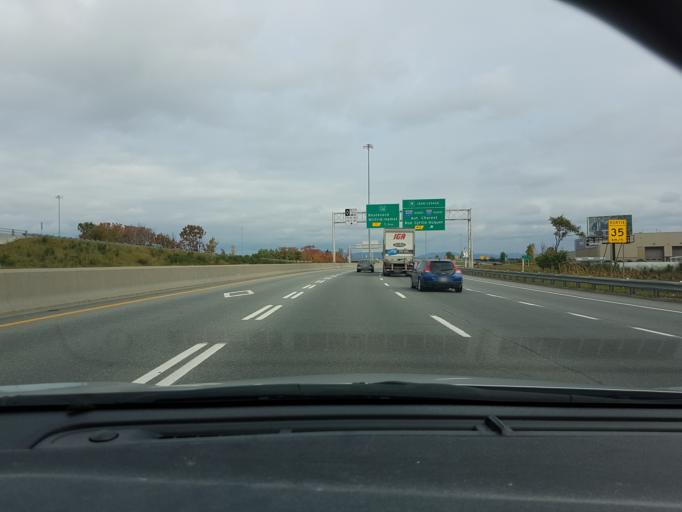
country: CA
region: Quebec
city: L'Ancienne-Lorette
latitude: 46.7958
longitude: -71.2878
